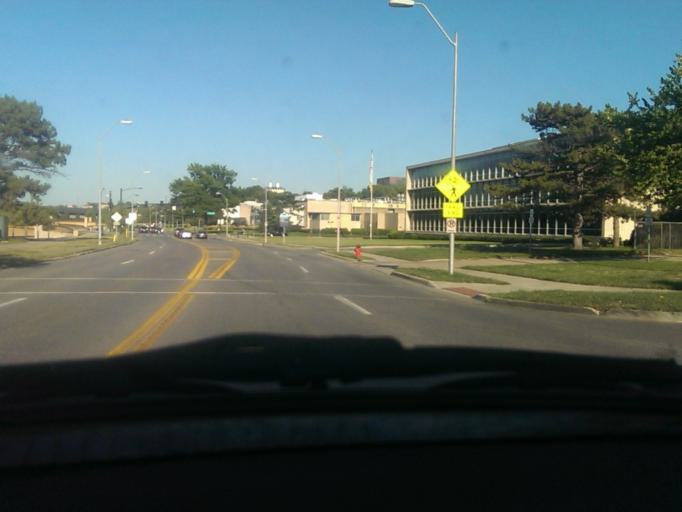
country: US
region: Kansas
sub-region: Johnson County
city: Westwood
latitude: 39.0389
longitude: -94.5844
